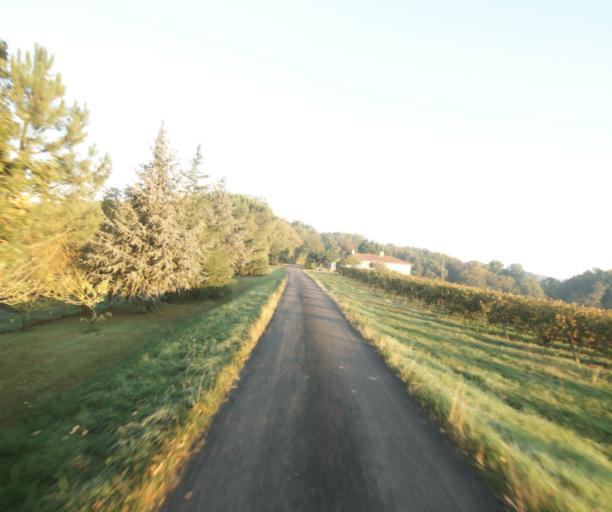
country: FR
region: Midi-Pyrenees
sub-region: Departement du Gers
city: Eauze
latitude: 43.7845
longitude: 0.1702
